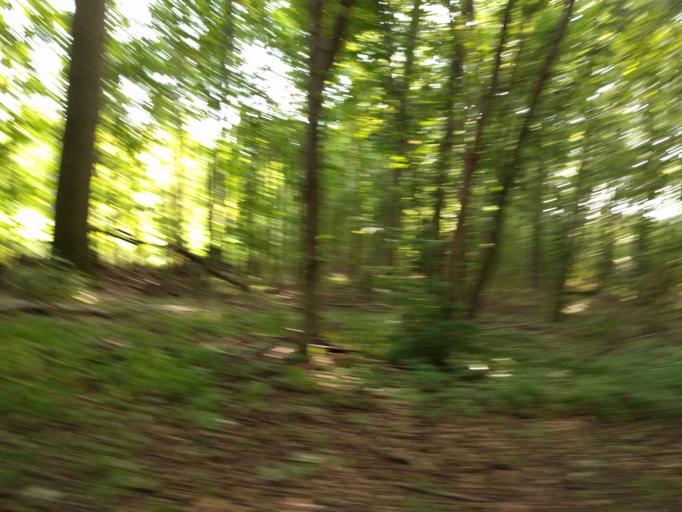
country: DK
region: South Denmark
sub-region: Odense Kommune
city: Odense
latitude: 55.4129
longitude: 10.3746
